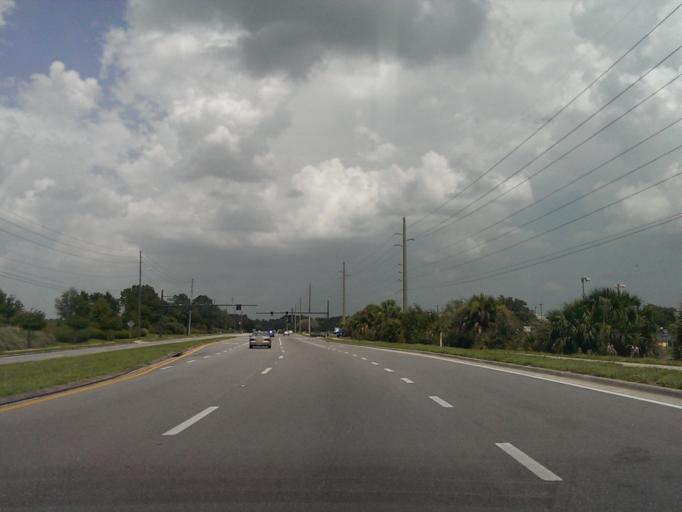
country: US
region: Florida
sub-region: Orange County
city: Doctor Phillips
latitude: 28.3985
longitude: -81.5303
